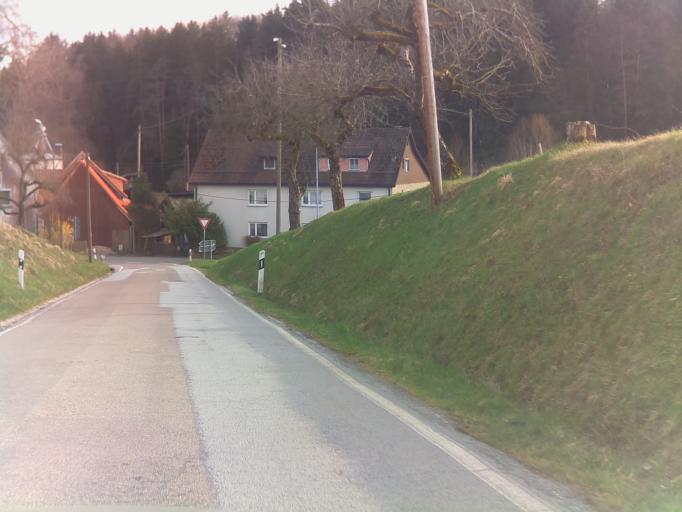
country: DE
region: Baden-Wuerttemberg
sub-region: Regierungsbezirk Stuttgart
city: Lorch
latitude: 48.8094
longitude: 9.6558
